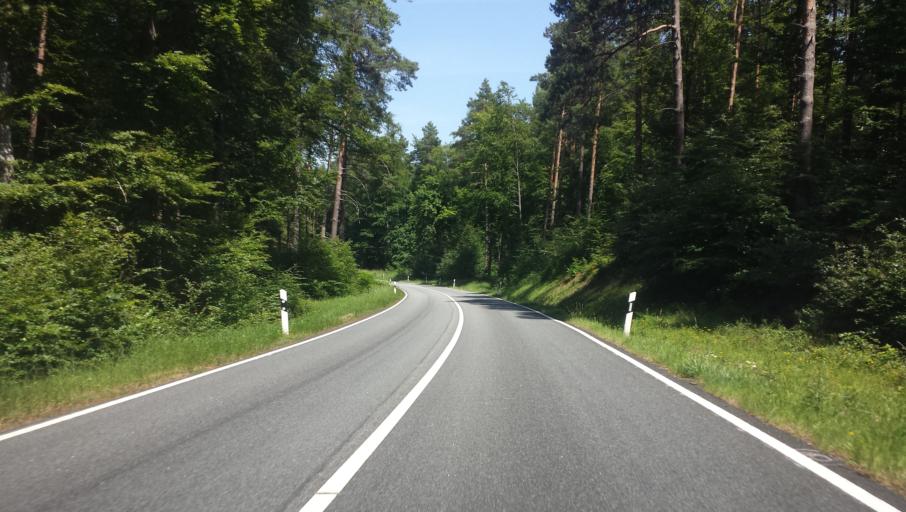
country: DE
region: Rheinland-Pfalz
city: Waldleiningen
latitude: 49.4218
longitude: 7.8862
